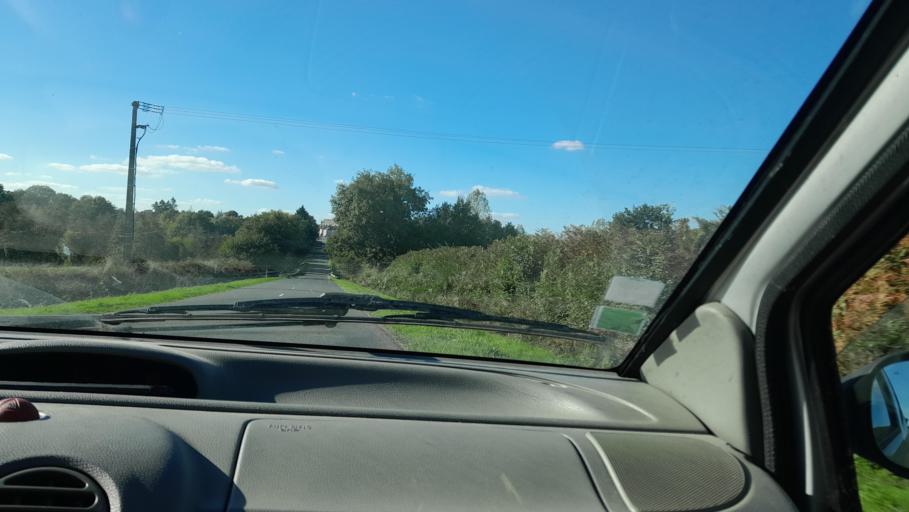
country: FR
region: Pays de la Loire
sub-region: Departement de la Mayenne
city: Cosse-le-Vivien
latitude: 47.9576
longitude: -0.9701
